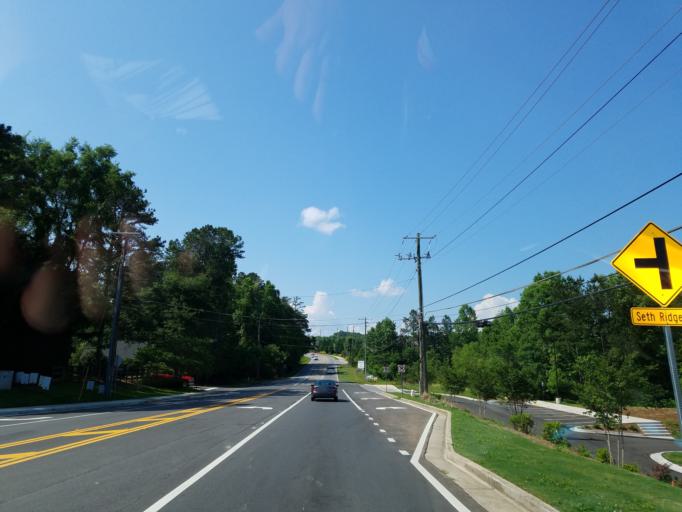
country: US
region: Georgia
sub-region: Cherokee County
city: Woodstock
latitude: 34.1314
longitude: -84.4977
